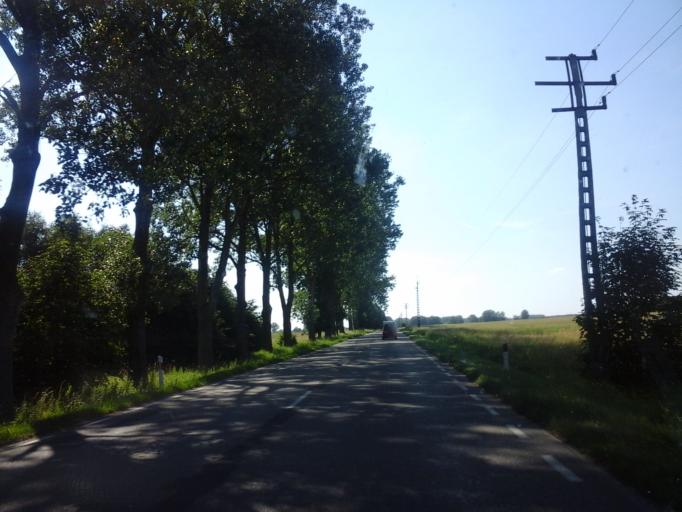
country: PL
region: West Pomeranian Voivodeship
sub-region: Powiat bialogardzki
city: Karlino
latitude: 54.0251
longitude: 15.9245
